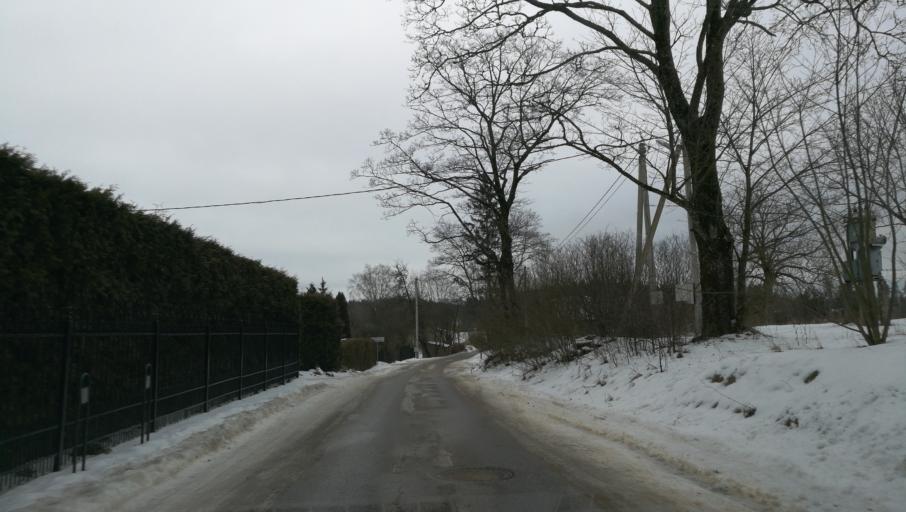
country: LT
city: Trakai
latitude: 54.6158
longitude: 24.9224
